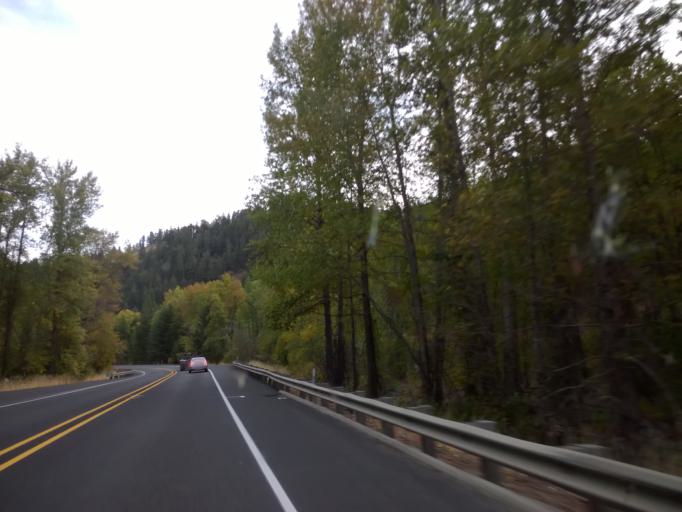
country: US
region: Washington
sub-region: Kittitas County
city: Cle Elum
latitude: 47.2166
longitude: -120.7003
